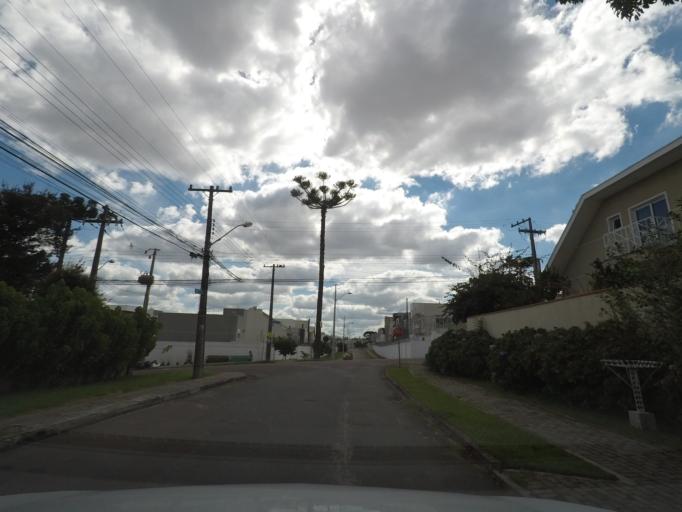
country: BR
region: Parana
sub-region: Sao Jose Dos Pinhais
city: Sao Jose dos Pinhais
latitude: -25.4824
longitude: -49.2355
